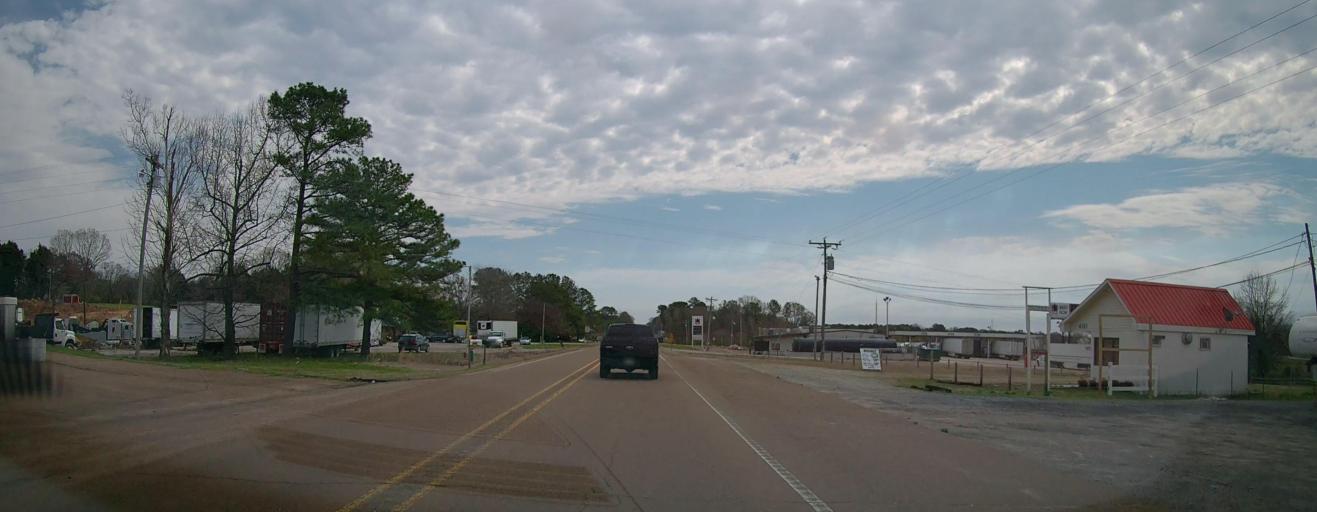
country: US
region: Mississippi
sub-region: Marshall County
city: Byhalia
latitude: 34.8291
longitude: -89.5677
